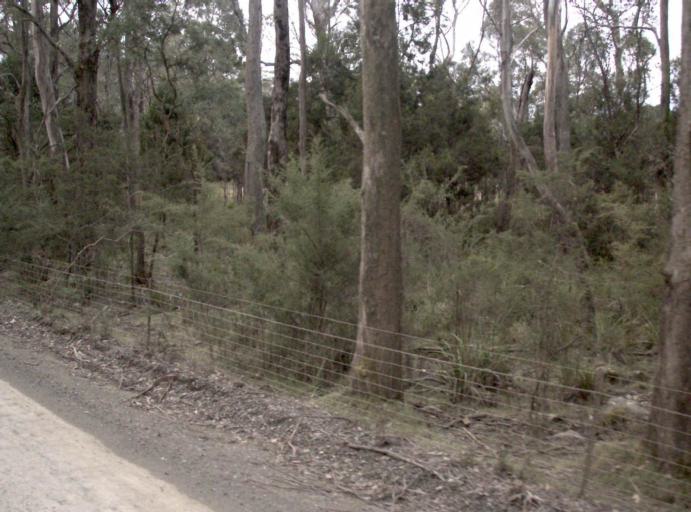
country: AU
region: Tasmania
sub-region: Launceston
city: Newstead
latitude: -41.3585
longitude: 147.2263
